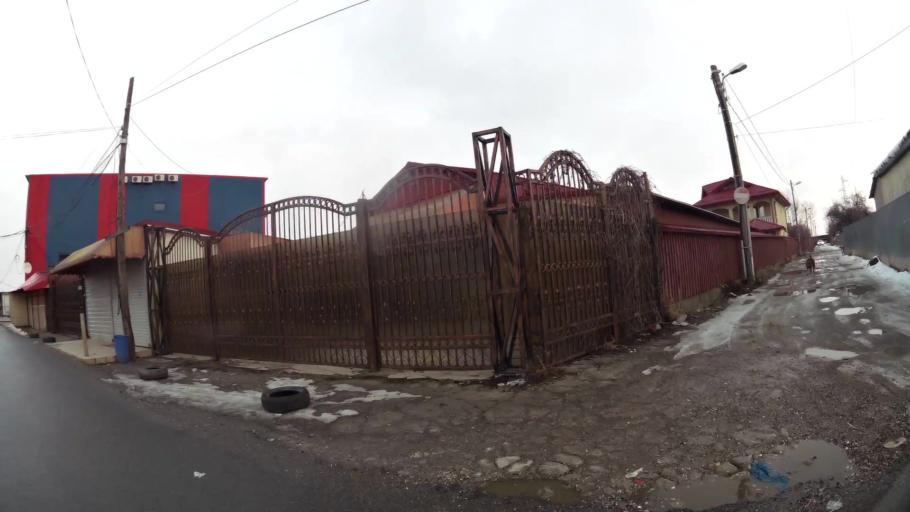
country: RO
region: Ilfov
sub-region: Voluntari City
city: Voluntari
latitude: 44.4779
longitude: 26.1719
